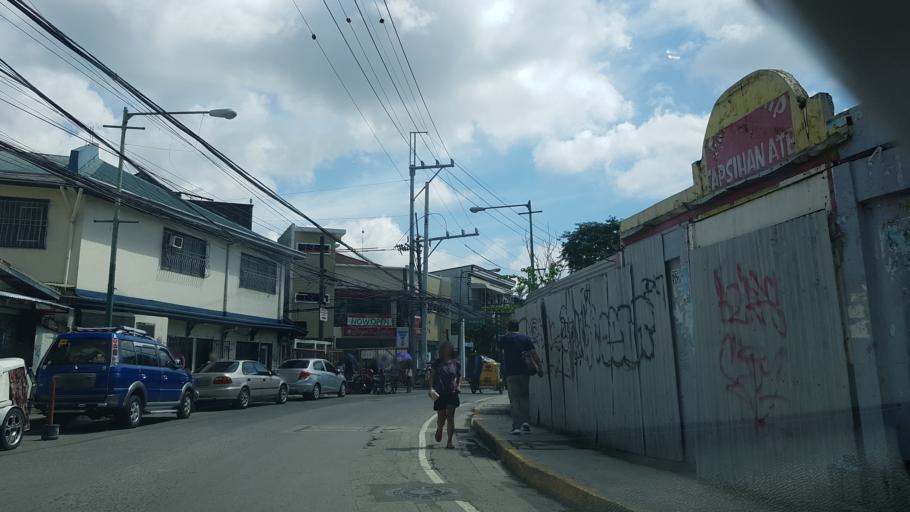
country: PH
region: Calabarzon
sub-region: Province of Rizal
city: Pateros
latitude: 14.5473
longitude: 121.0619
